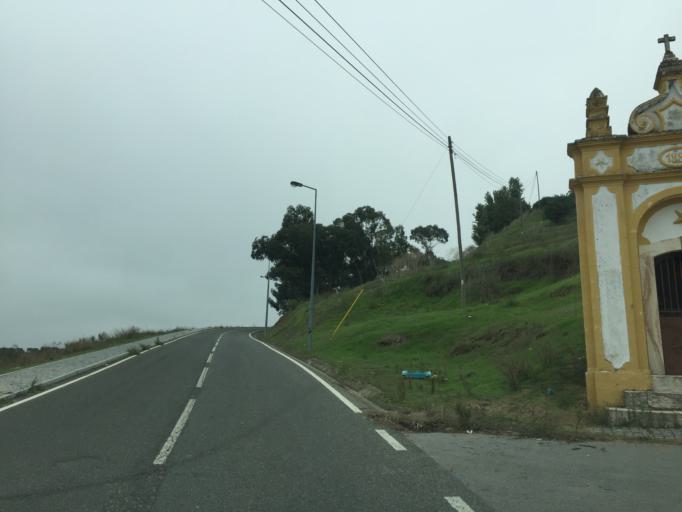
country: PT
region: Portalegre
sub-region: Arronches
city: Arronches
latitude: 39.0541
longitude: -7.4416
